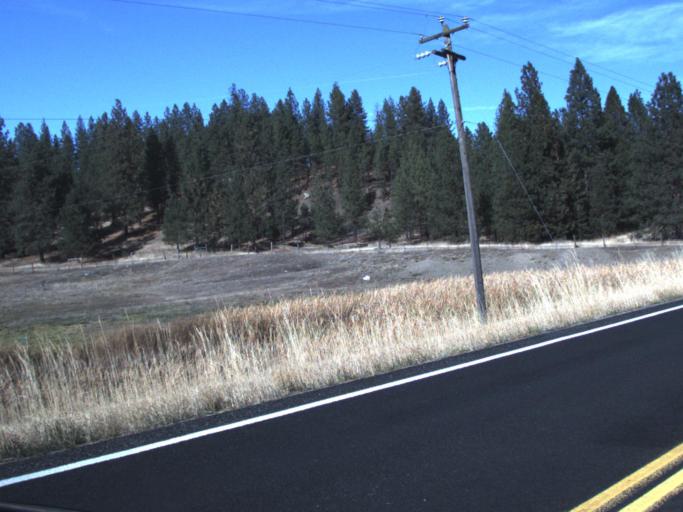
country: US
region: Washington
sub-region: Lincoln County
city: Davenport
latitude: 47.9830
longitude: -118.2933
